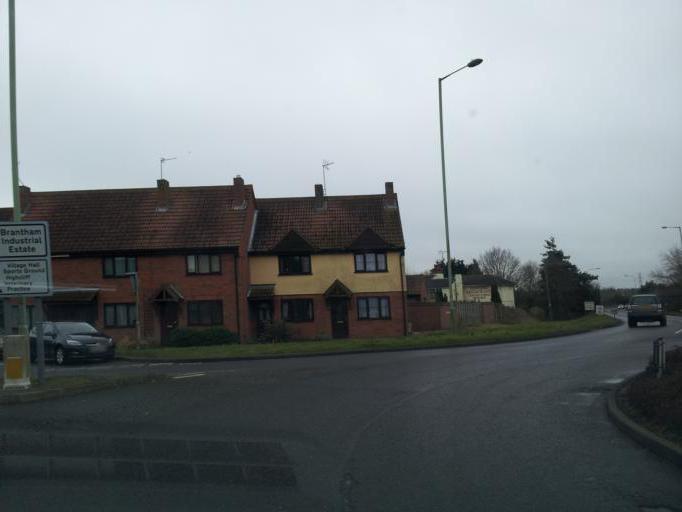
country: GB
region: England
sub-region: Essex
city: Manningtree
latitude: 51.9576
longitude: 1.0570
